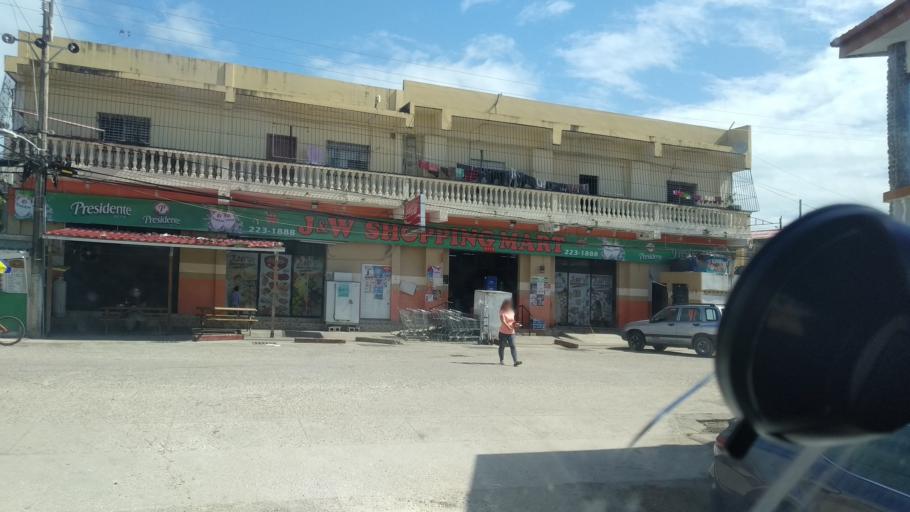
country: BZ
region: Belize
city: Belize City
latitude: 17.5079
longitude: -88.1924
